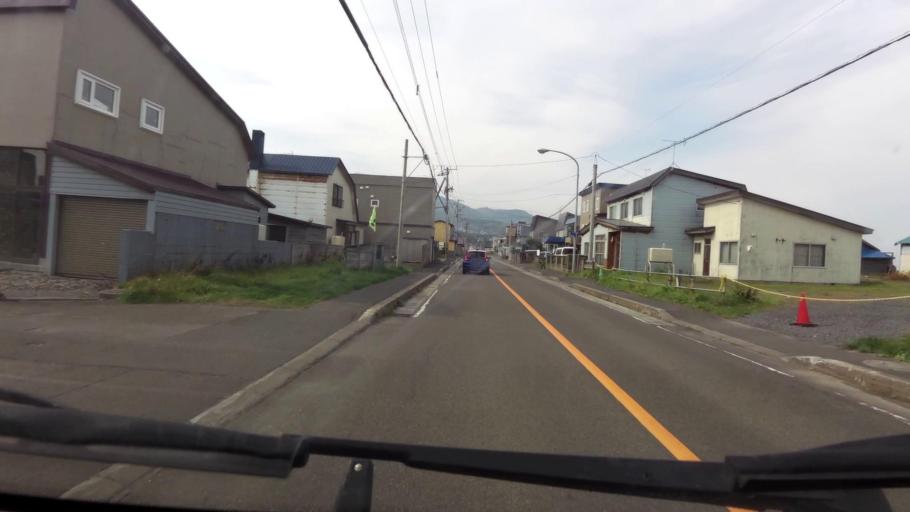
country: JP
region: Hokkaido
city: Otaru
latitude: 43.1453
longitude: 141.1708
